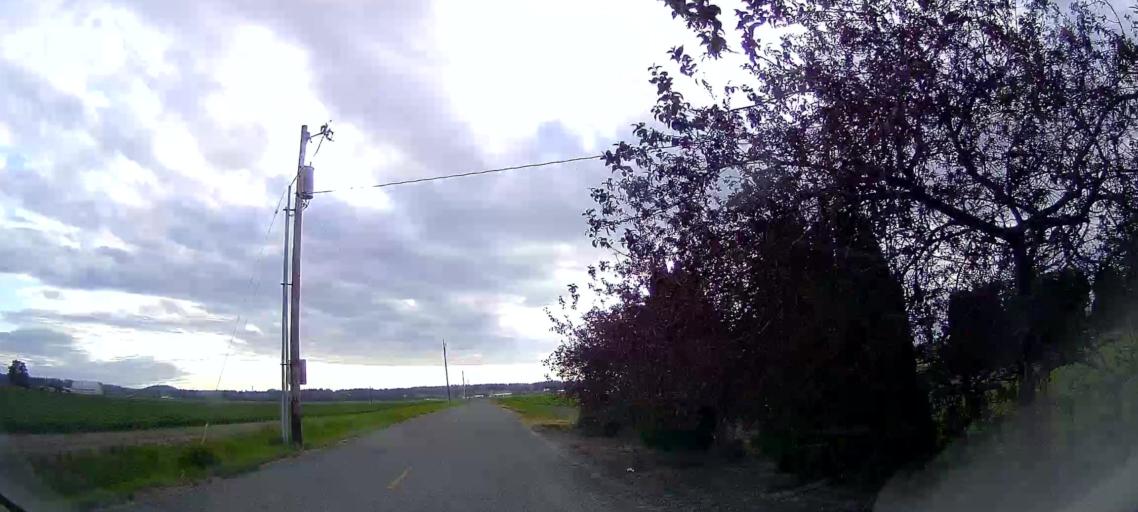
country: US
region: Washington
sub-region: Skagit County
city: Mount Vernon
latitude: 48.3848
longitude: -122.3947
